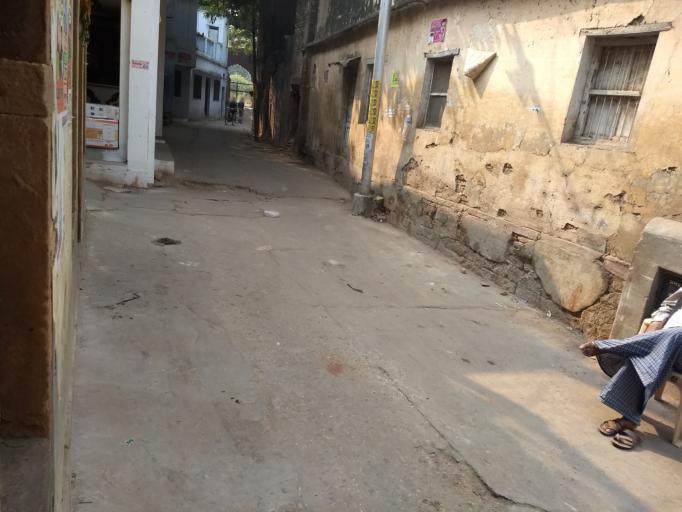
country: IN
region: Uttar Pradesh
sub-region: Mirzapur
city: Mirzapur
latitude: 25.1510
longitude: 82.5622
